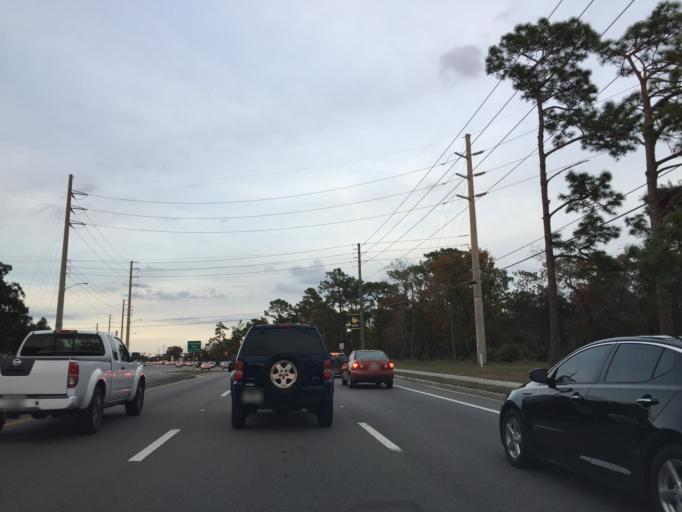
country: US
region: Florida
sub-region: Orange County
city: Alafaya
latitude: 28.5941
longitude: -81.2085
